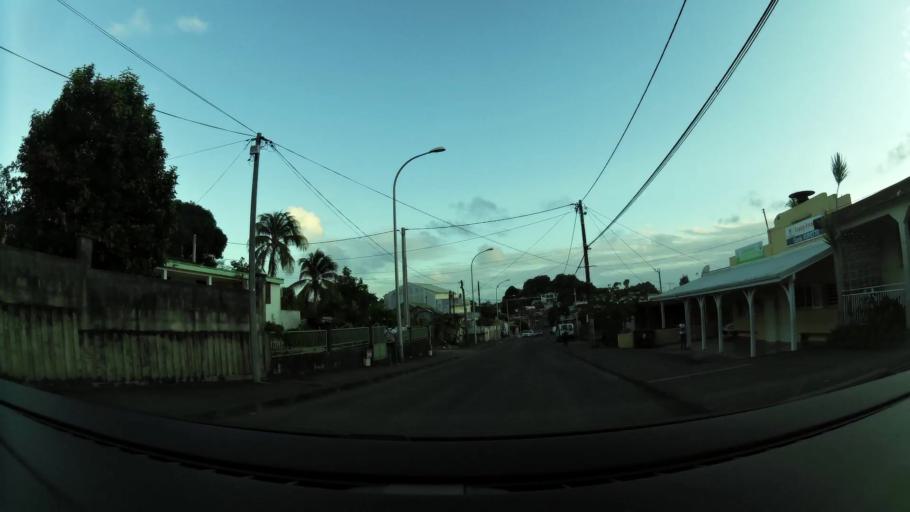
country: GP
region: Guadeloupe
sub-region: Guadeloupe
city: Les Abymes
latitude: 16.2689
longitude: -61.5031
